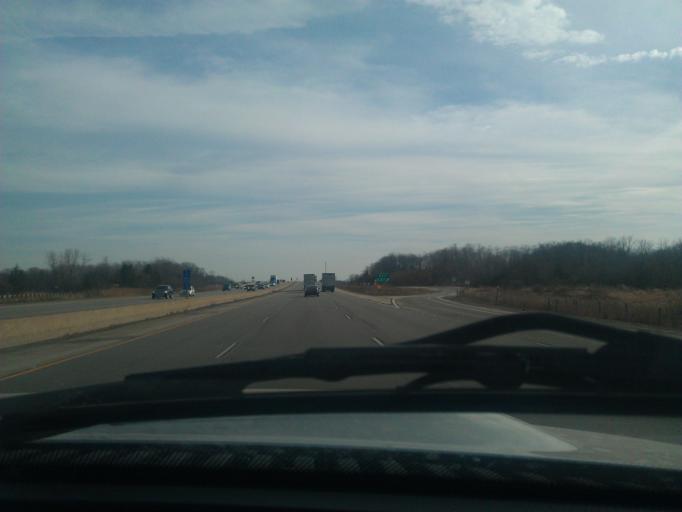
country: US
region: Wisconsin
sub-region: Kenosha County
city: Somers
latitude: 42.6745
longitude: -87.9531
